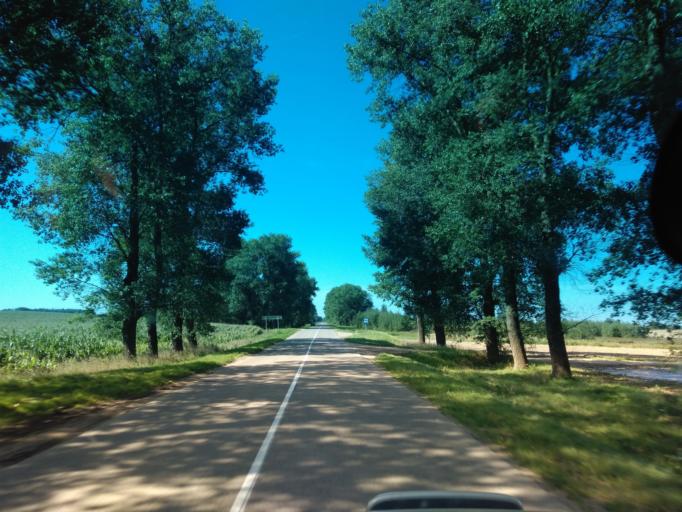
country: BY
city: Fanipol
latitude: 53.6575
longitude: 27.3198
